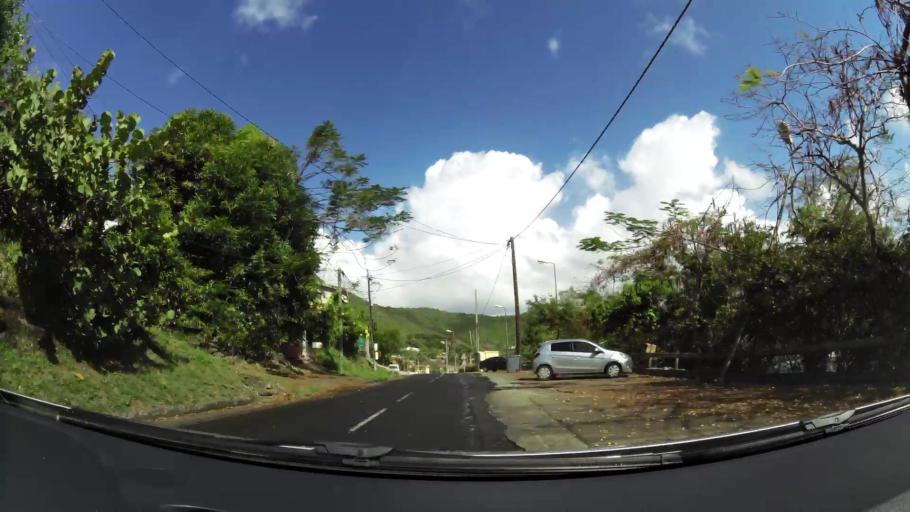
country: MQ
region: Martinique
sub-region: Martinique
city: Les Trois-Ilets
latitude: 14.4660
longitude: -61.0470
